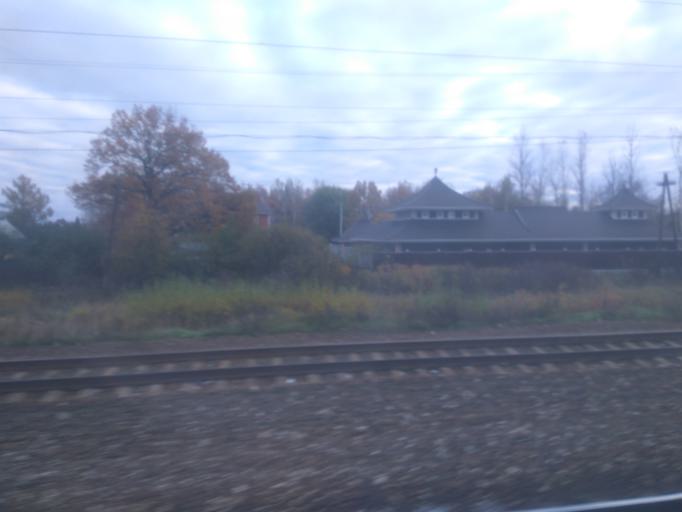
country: RU
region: Moskovskaya
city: Aprelevka
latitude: 55.5794
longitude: 37.1138
